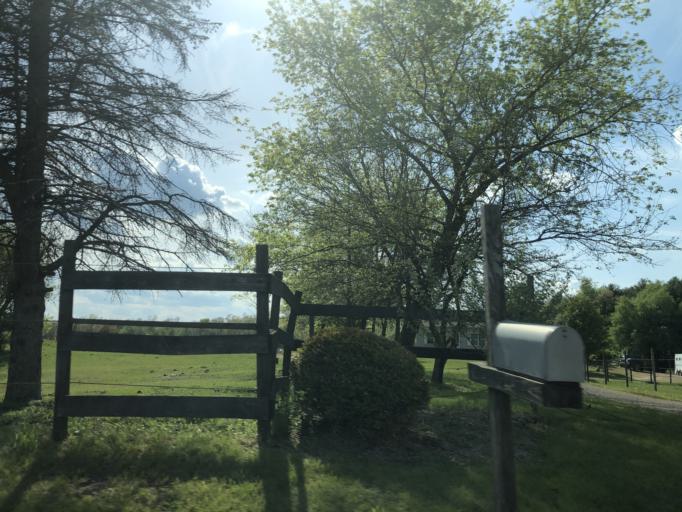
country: US
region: Michigan
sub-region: Hillsdale County
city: Reading
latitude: 41.7555
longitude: -84.8098
